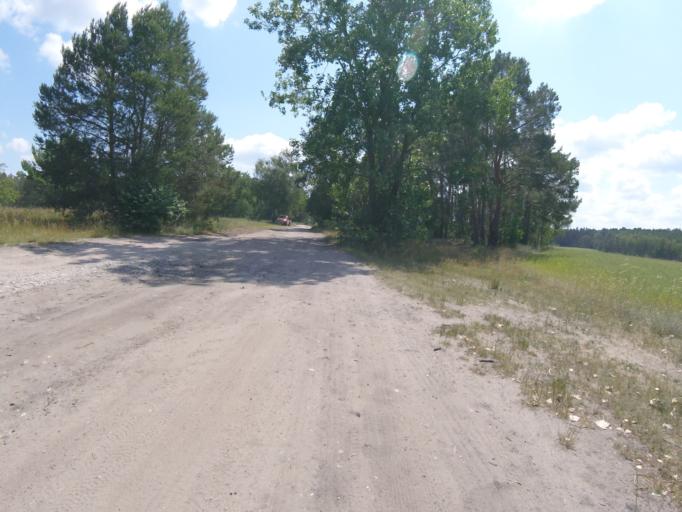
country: DE
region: Brandenburg
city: Bestensee
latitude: 52.2814
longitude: 13.6762
